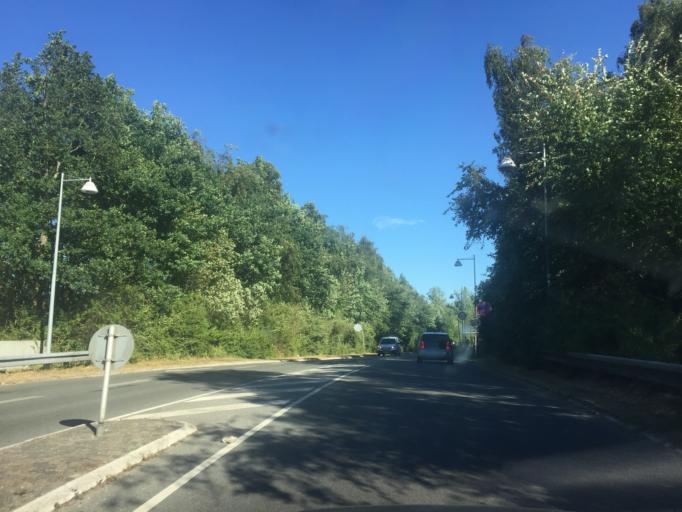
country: DK
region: Capital Region
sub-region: Albertslund Kommune
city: Albertslund
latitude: 55.6722
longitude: 12.3458
